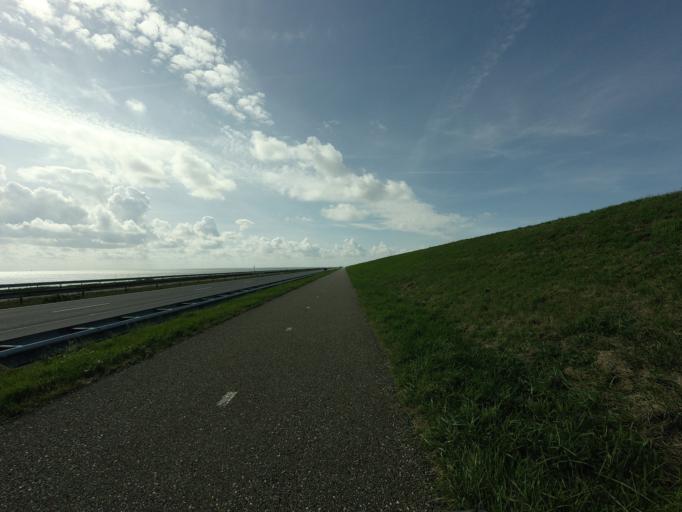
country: NL
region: North Holland
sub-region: Gemeente Hollands Kroon
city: Den Oever
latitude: 52.9965
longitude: 5.1604
